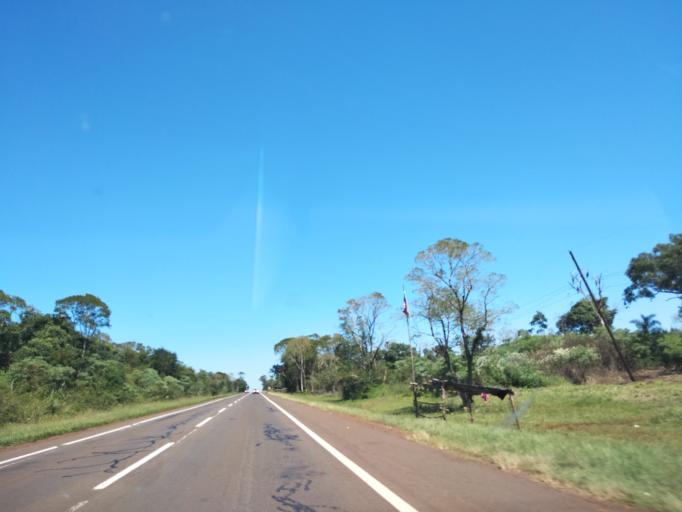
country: AR
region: Misiones
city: Puerto Libertad
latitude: -25.7705
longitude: -54.5379
